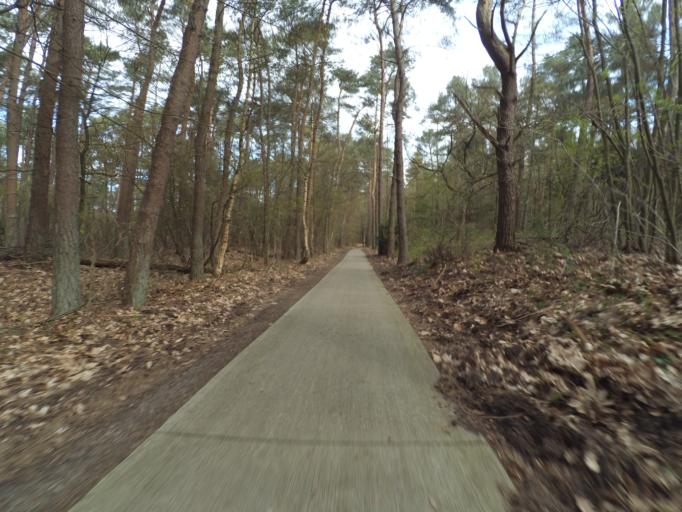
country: NL
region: Gelderland
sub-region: Gemeente Nunspeet
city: Nunspeet
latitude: 52.3540
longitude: 5.7572
